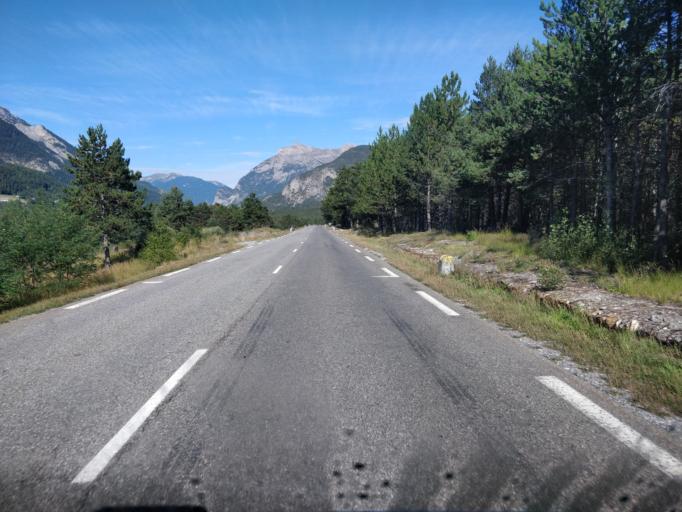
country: FR
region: Provence-Alpes-Cote d'Azur
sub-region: Departement des Alpes-de-Haute-Provence
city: Barcelonnette
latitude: 44.3872
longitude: 6.6002
